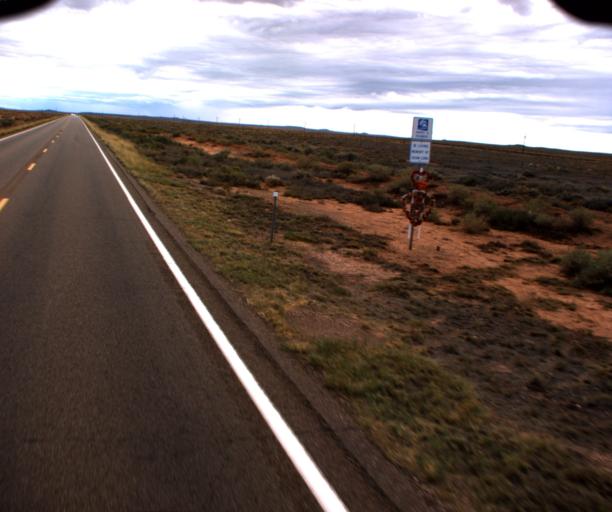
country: US
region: Arizona
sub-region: Navajo County
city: Holbrook
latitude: 34.8112
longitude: -110.1382
